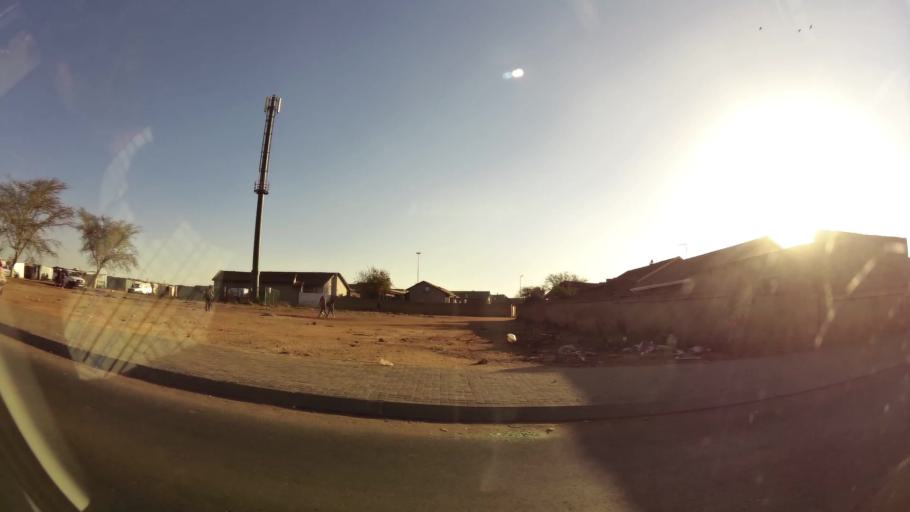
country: ZA
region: Gauteng
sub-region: Ekurhuleni Metropolitan Municipality
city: Tembisa
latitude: -26.0147
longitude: 28.2303
